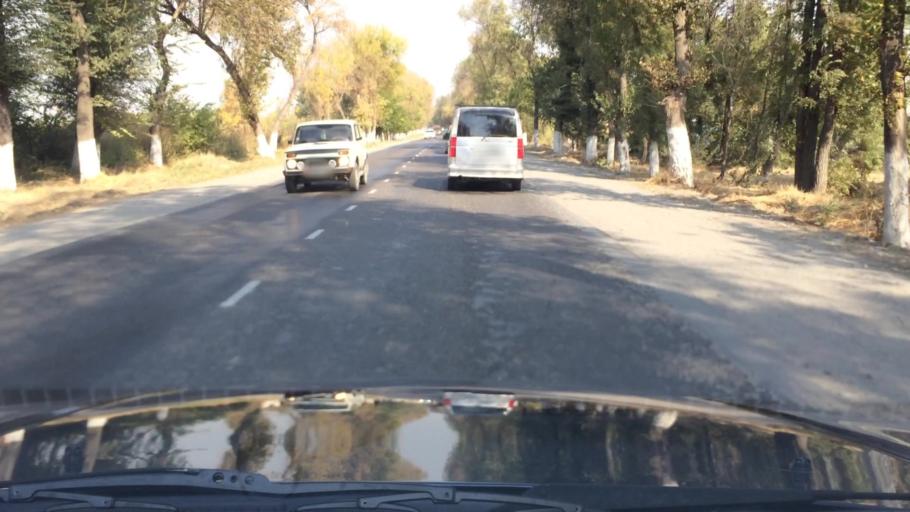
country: KG
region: Chuy
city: Lebedinovka
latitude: 42.9225
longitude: 74.6899
